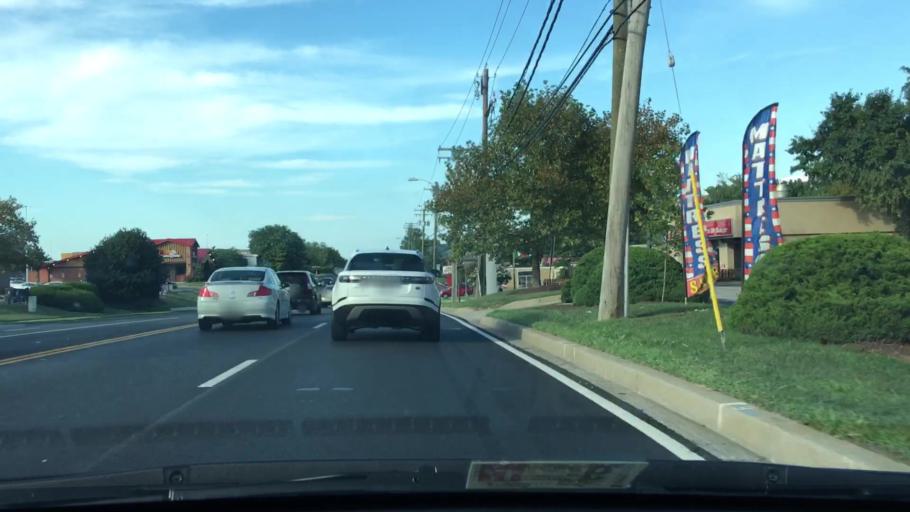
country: US
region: Maryland
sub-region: Prince George's County
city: South Laurel
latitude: 39.0825
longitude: -76.8634
